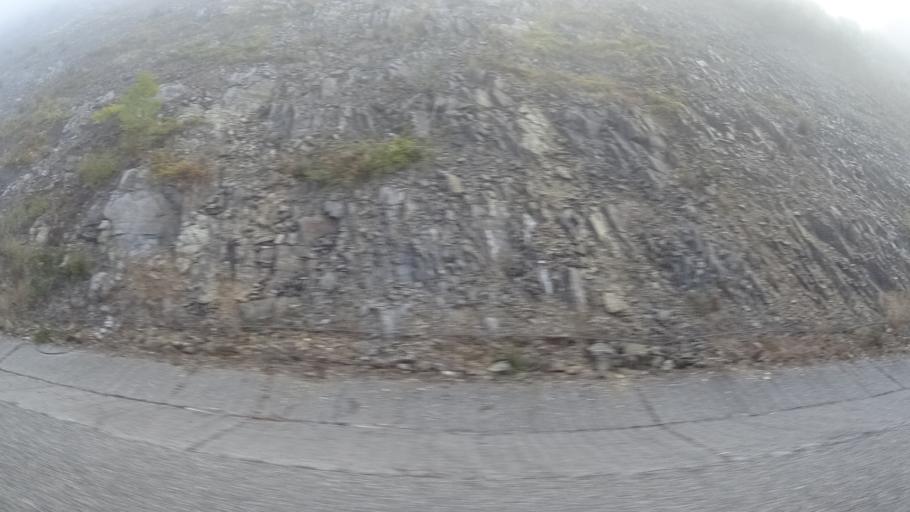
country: ES
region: Galicia
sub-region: Provincia de Lugo
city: Becerrea
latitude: 42.7975
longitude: -7.1077
